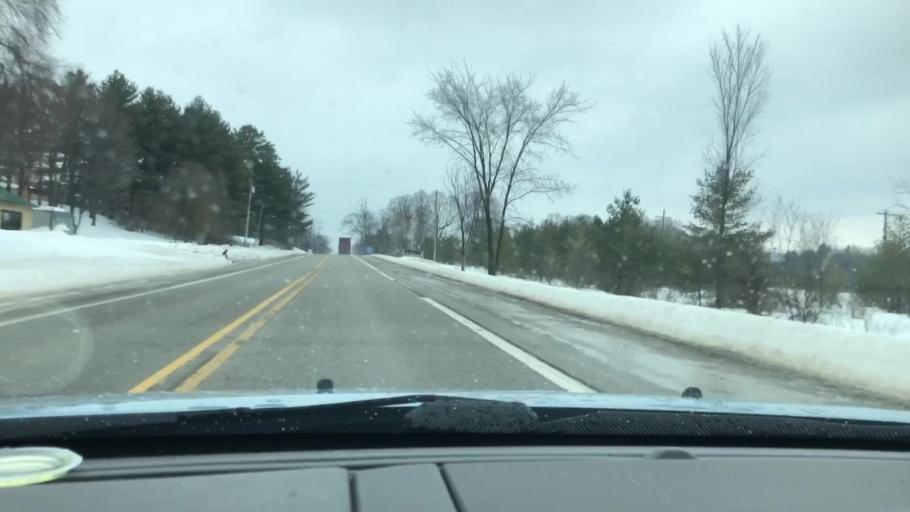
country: US
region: Michigan
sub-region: Charlevoix County
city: East Jordan
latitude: 45.1414
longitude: -85.1398
